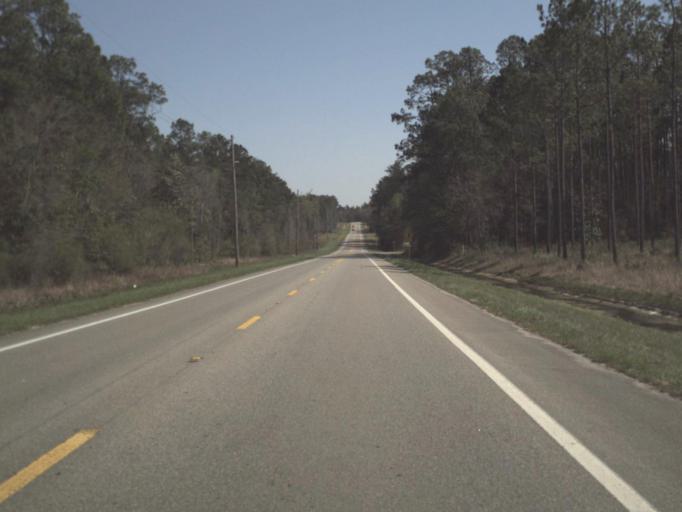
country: US
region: Florida
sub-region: Liberty County
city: Bristol
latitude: 30.3991
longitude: -84.8122
